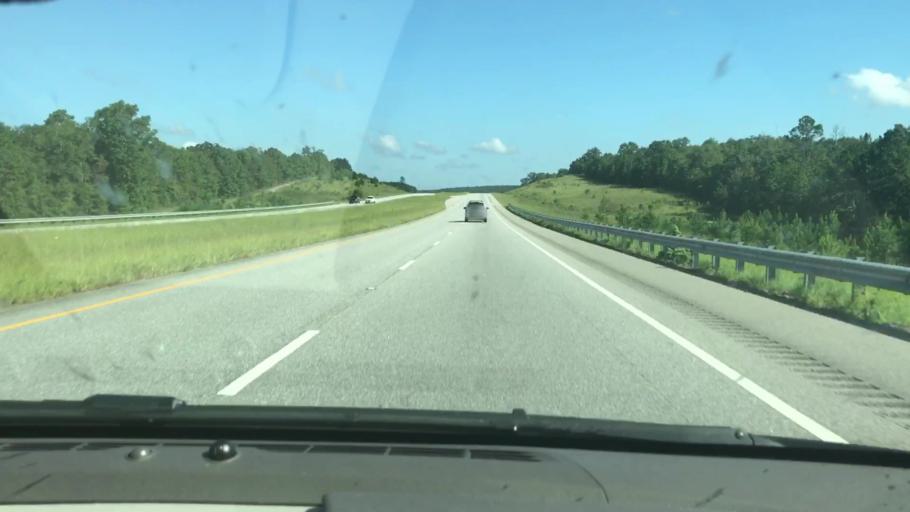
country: US
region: Alabama
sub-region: Barbour County
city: Eufaula
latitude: 32.1019
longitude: -85.1500
